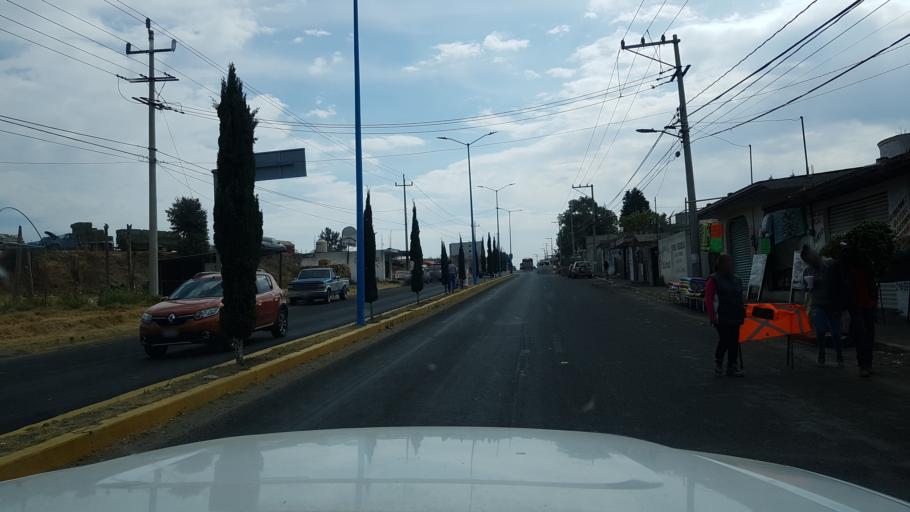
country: MX
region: Puebla
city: San Martin Texmelucan de Labastida
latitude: 19.2937
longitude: -98.4049
